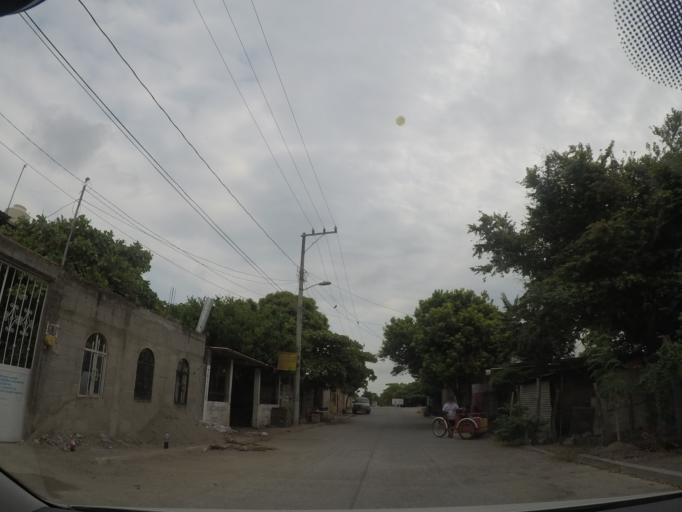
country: MX
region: Oaxaca
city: Juchitan de Zaragoza
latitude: 16.4576
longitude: -95.0156
